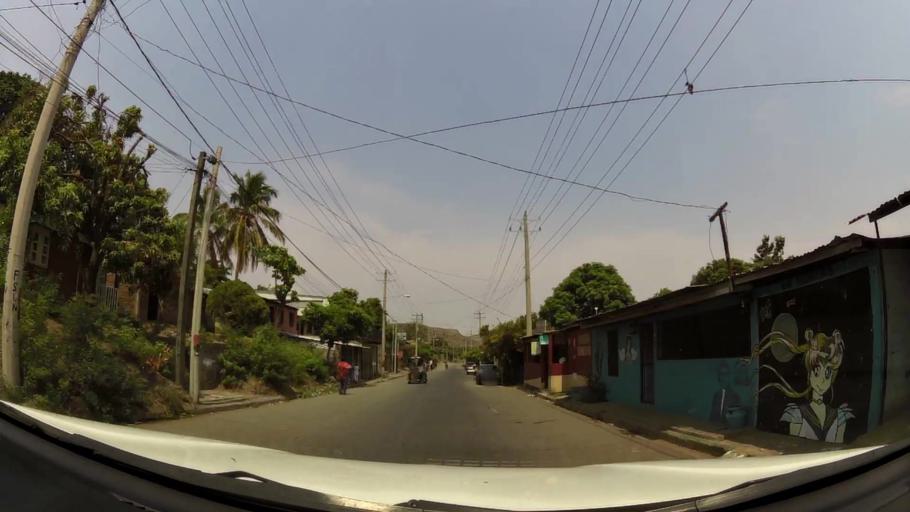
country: NI
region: Managua
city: Ciudad Sandino
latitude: 12.1590
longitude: -86.3072
